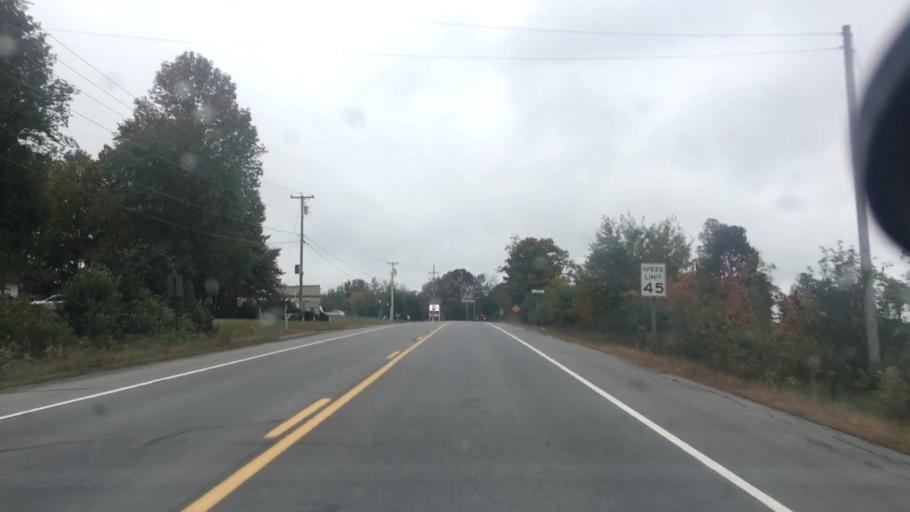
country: US
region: Maine
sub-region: Kennebec County
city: Belgrade
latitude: 44.3979
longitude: -69.8052
